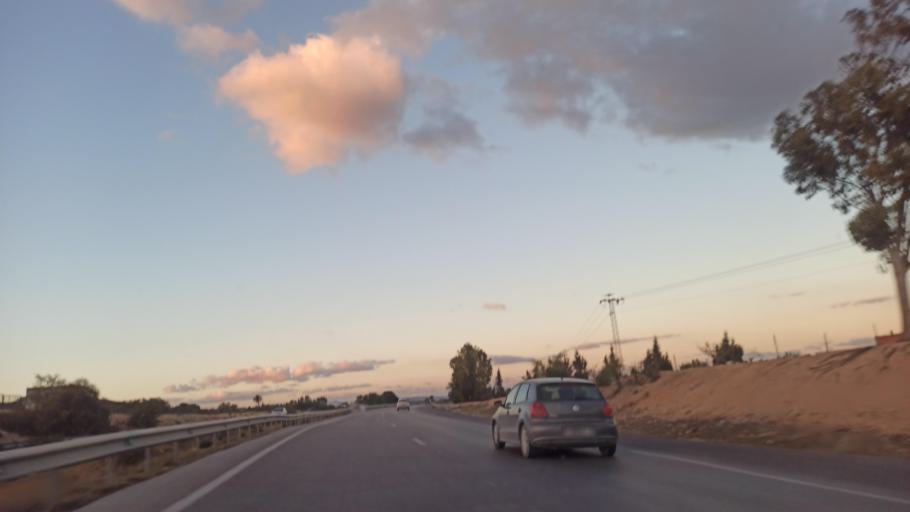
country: TN
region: Susah
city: Harqalah
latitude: 36.2305
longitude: 10.4131
